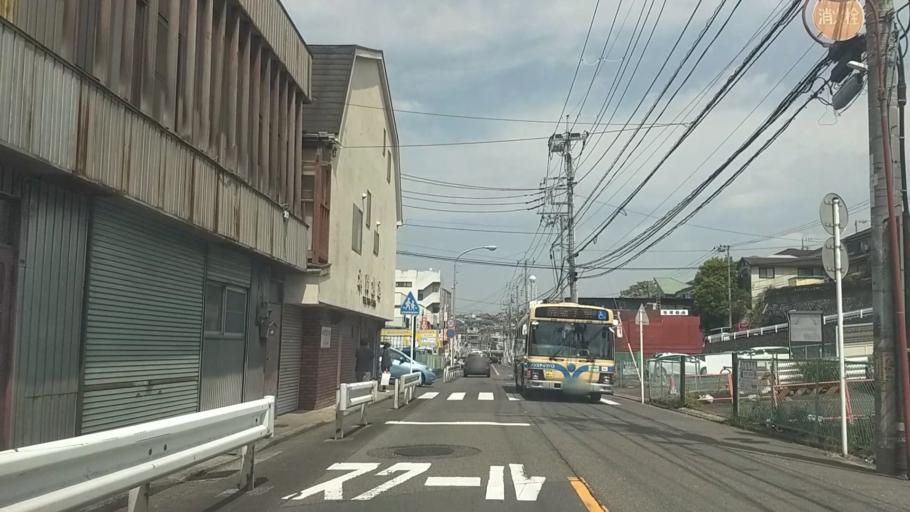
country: JP
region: Kanagawa
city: Yokohama
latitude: 35.4114
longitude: 139.6097
